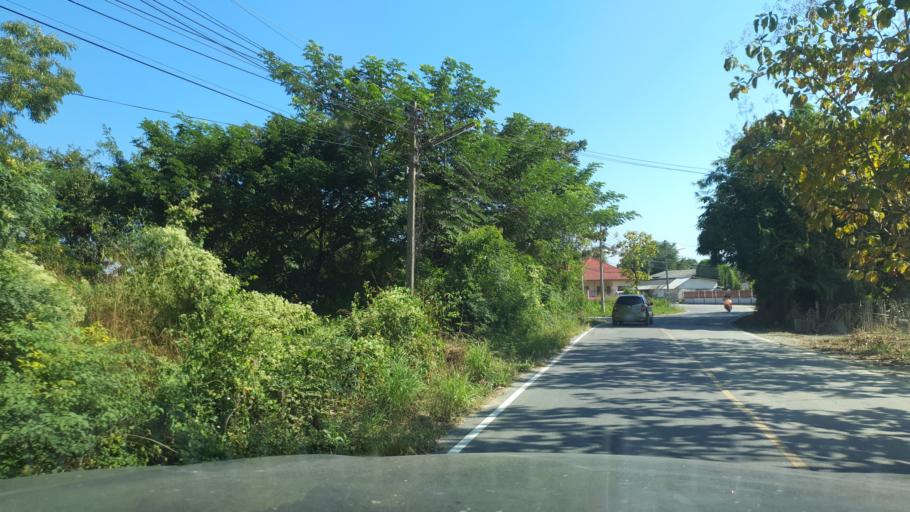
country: TH
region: Chiang Mai
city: San Sai
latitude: 18.8134
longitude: 99.0806
